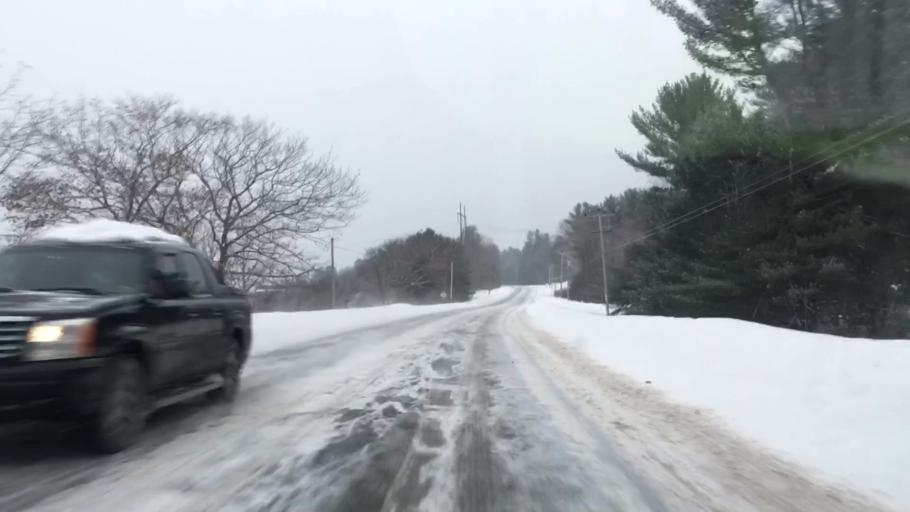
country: US
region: Maine
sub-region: Penobscot County
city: Medway
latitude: 45.5665
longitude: -68.4014
